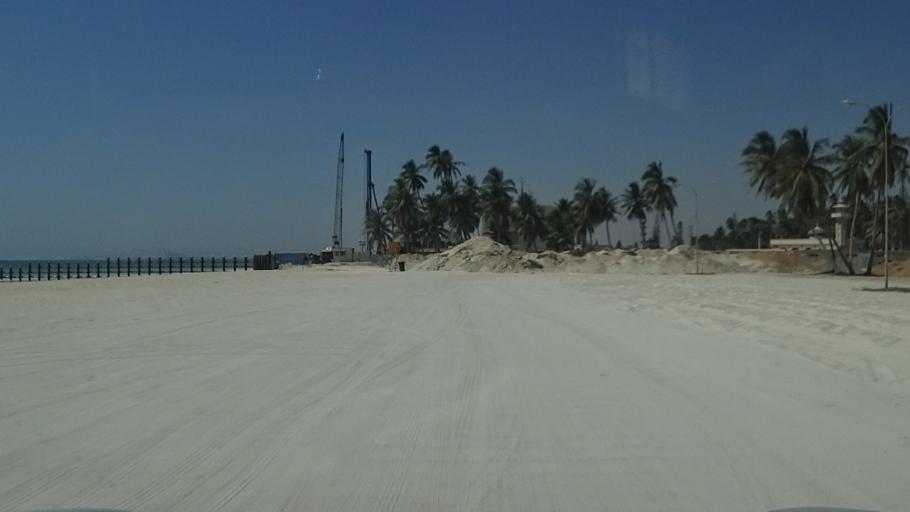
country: OM
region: Zufar
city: Salalah
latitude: 16.9997
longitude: 54.1028
